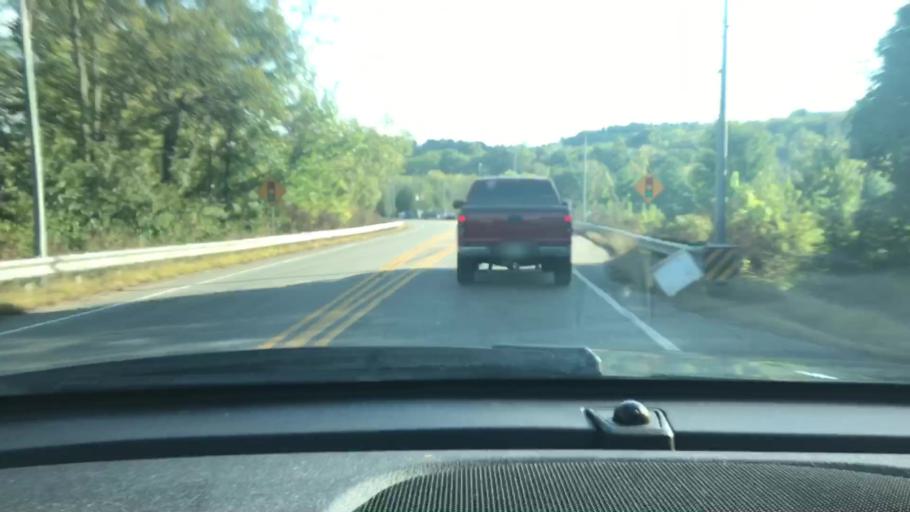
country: US
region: Tennessee
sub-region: Sumner County
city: Shackle Island
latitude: 36.3726
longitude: -86.6170
